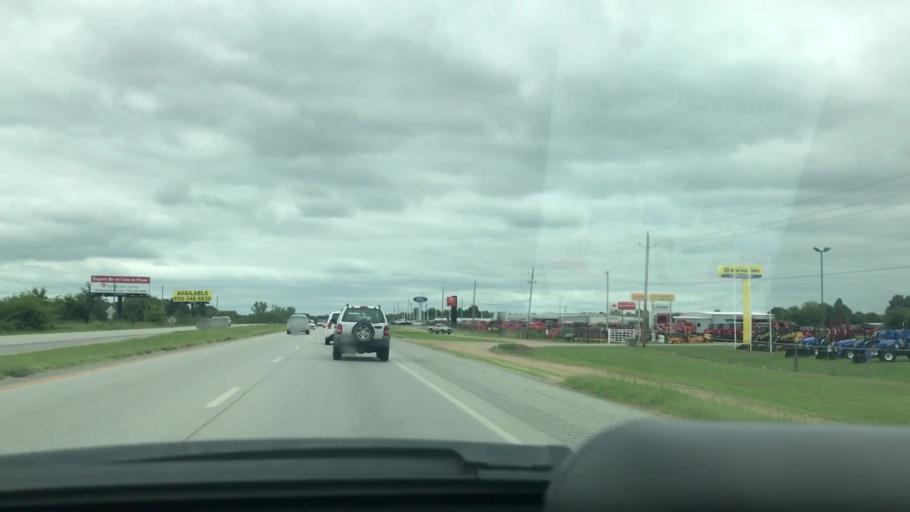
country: US
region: Oklahoma
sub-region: Mayes County
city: Pryor
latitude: 36.2646
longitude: -95.3328
